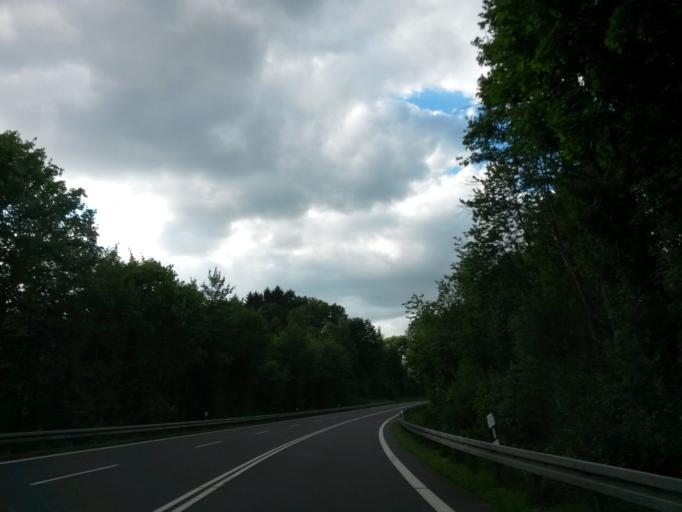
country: DE
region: North Rhine-Westphalia
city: Waldbrol
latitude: 50.9244
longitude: 7.6319
